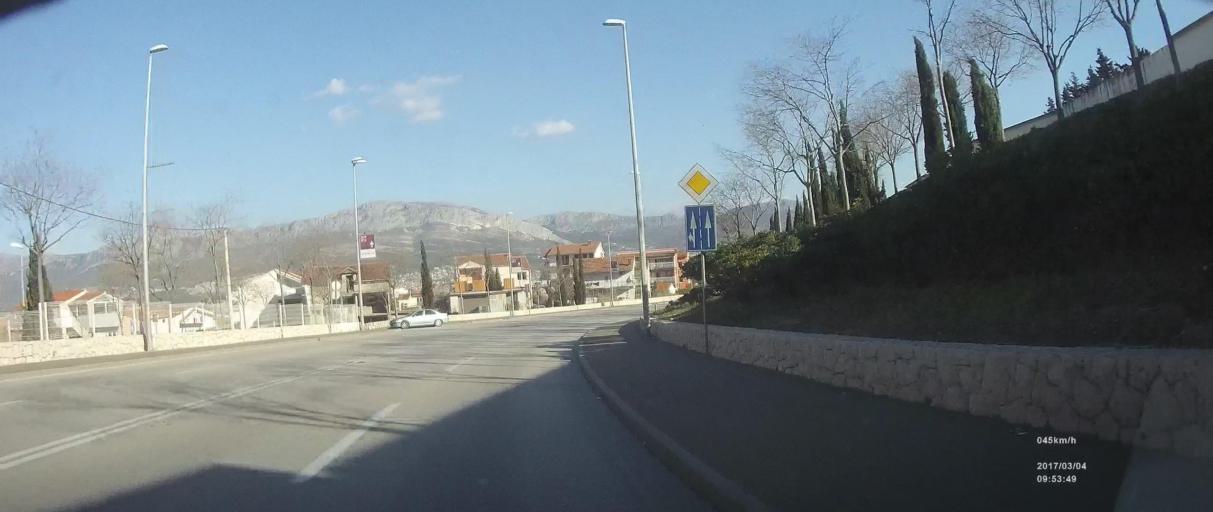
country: HR
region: Splitsko-Dalmatinska
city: Kamen
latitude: 43.5126
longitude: 16.4900
